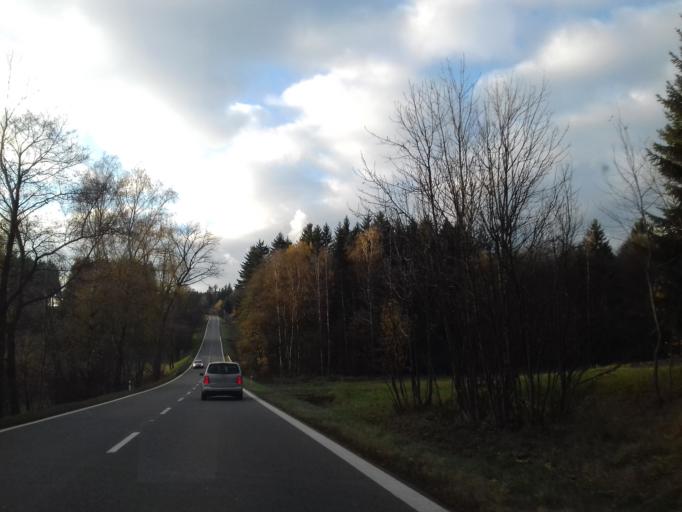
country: CZ
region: Pardubicky
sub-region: Okres Svitavy
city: Policka
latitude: 49.7410
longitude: 16.1993
